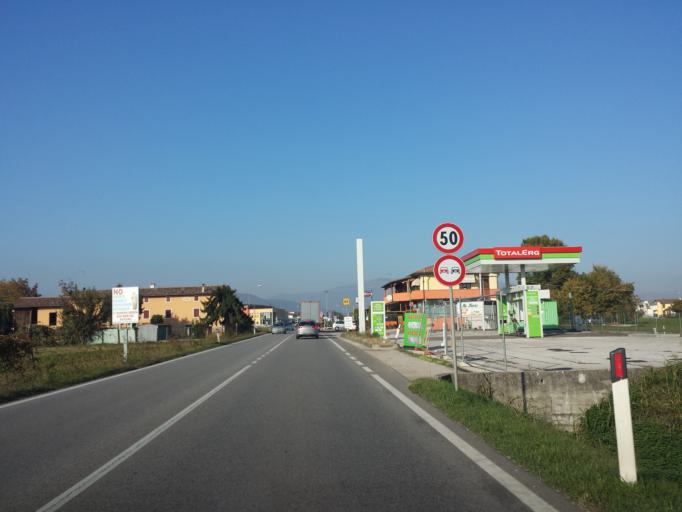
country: IT
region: Veneto
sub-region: Provincia di Treviso
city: Caerano di San Marco
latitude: 45.7768
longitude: 11.9937
